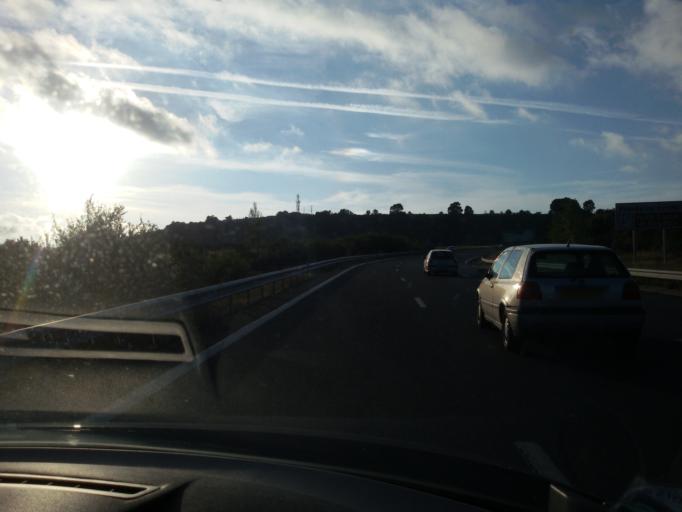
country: FR
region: Languedoc-Roussillon
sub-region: Departement de l'Herault
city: Lodeve
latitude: 43.8475
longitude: 3.3080
